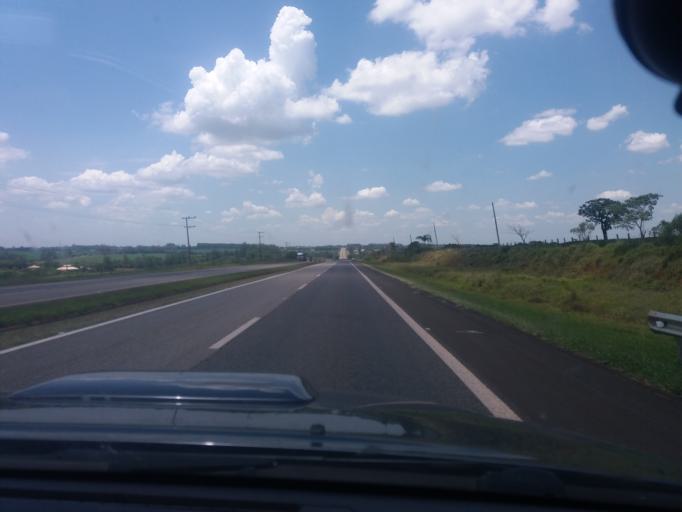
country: BR
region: Sao Paulo
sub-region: Itapetininga
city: Itapetininga
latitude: -23.5570
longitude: -47.9716
